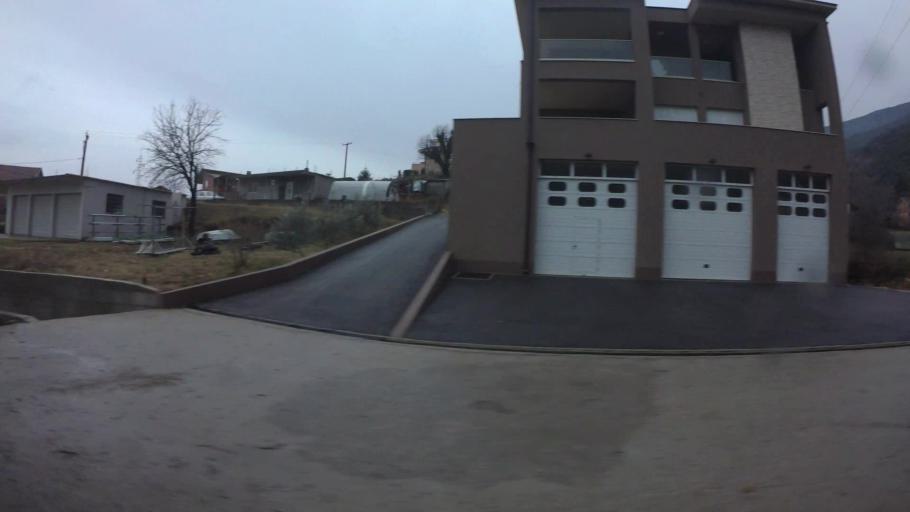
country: BA
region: Federation of Bosnia and Herzegovina
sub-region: Hercegovacko-Bosanski Kanton
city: Mostar
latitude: 43.3682
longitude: 17.8078
